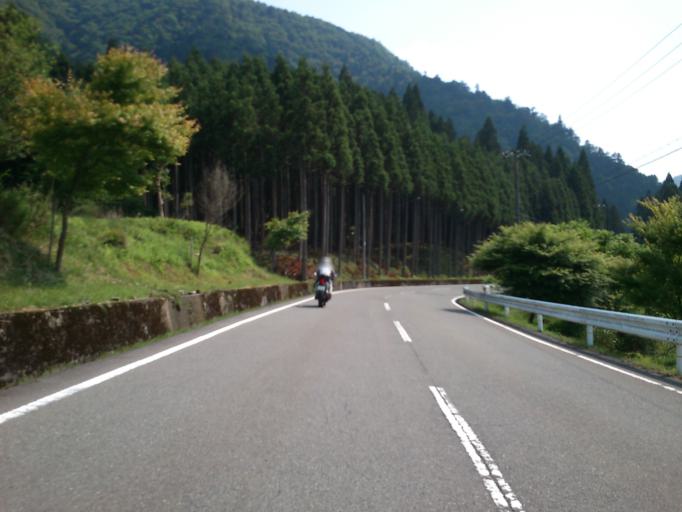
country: JP
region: Kyoto
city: Kameoka
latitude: 35.2599
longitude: 135.5715
